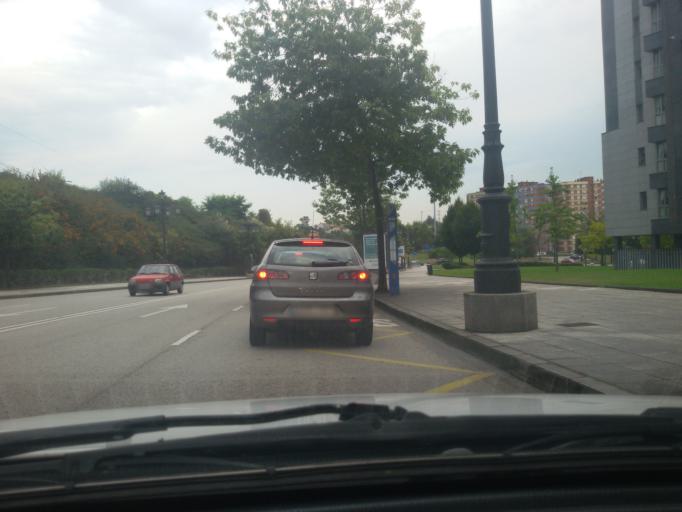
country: ES
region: Asturias
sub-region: Province of Asturias
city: Oviedo
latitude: 43.3716
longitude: -5.8479
